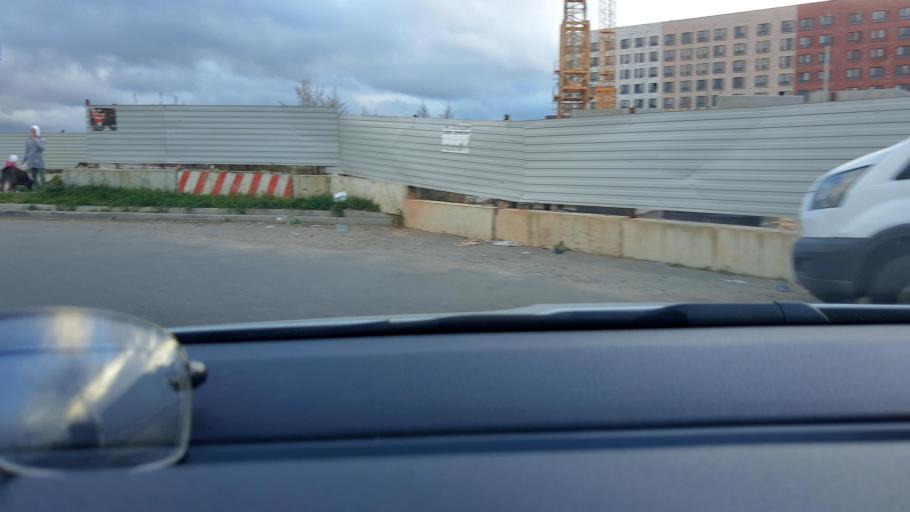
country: RU
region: Moskovskaya
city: Opalikha
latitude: 55.7754
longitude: 37.2377
